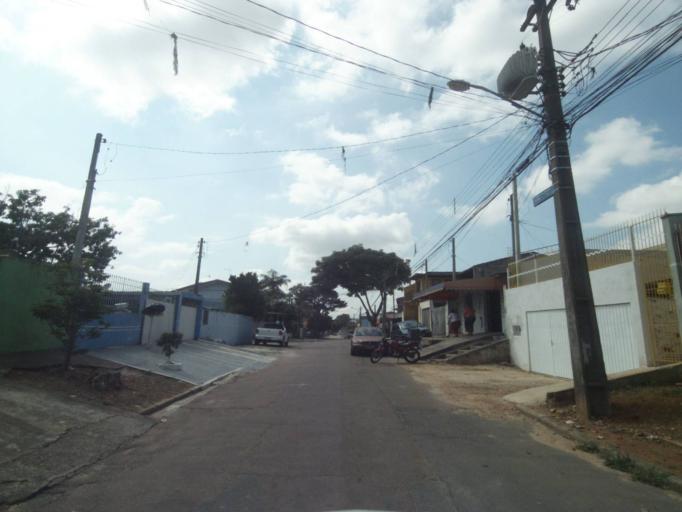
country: BR
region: Parana
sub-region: Sao Jose Dos Pinhais
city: Sao Jose dos Pinhais
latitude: -25.5427
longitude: -49.2663
